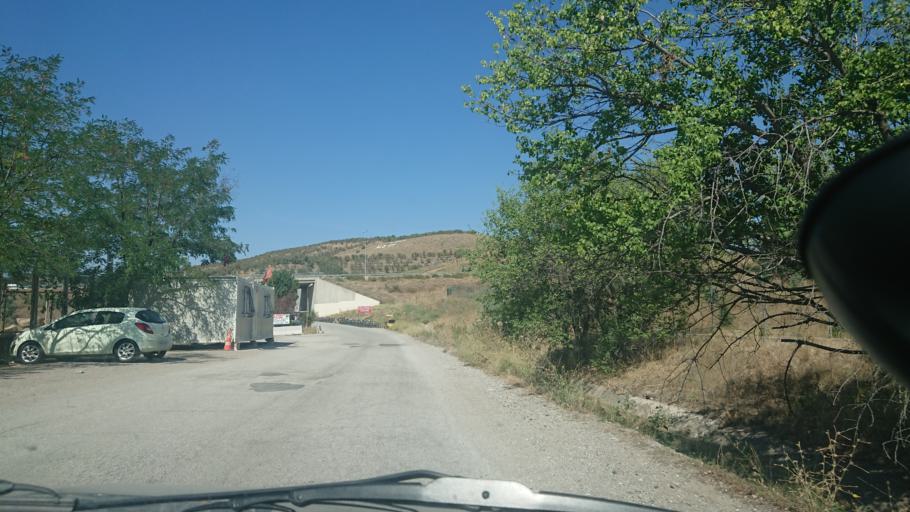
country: TR
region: Ankara
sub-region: Goelbasi
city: Golbasi
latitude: 39.8113
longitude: 32.8215
